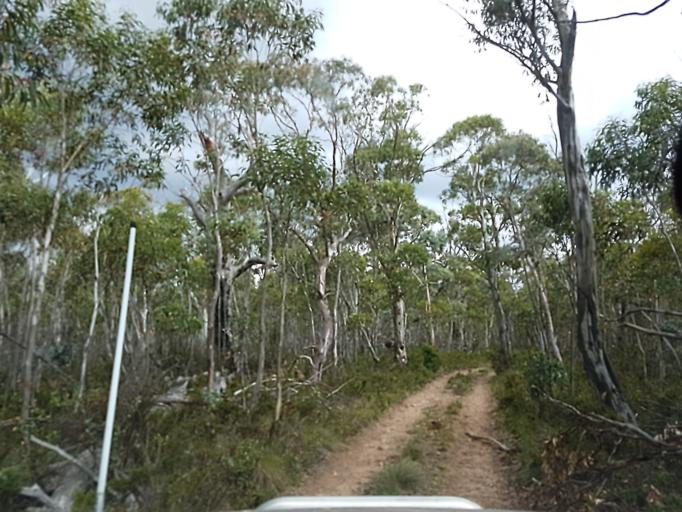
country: AU
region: New South Wales
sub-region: Snowy River
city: Jindabyne
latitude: -36.8784
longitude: 148.1807
